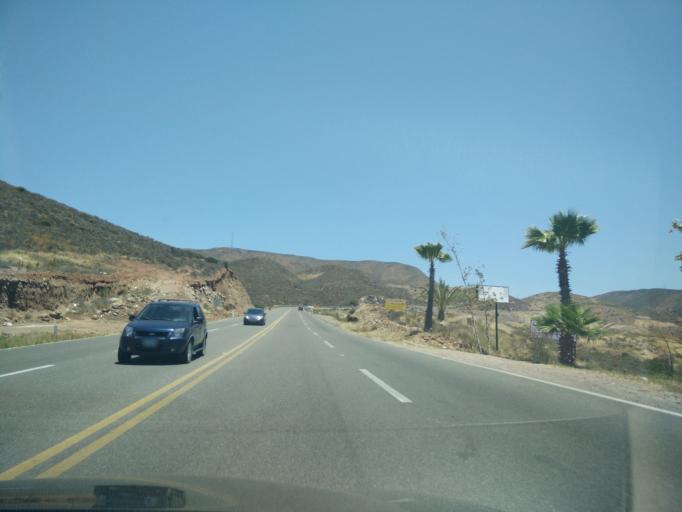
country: MX
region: Baja California
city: El Sauzal
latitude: 31.9254
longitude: -116.6752
